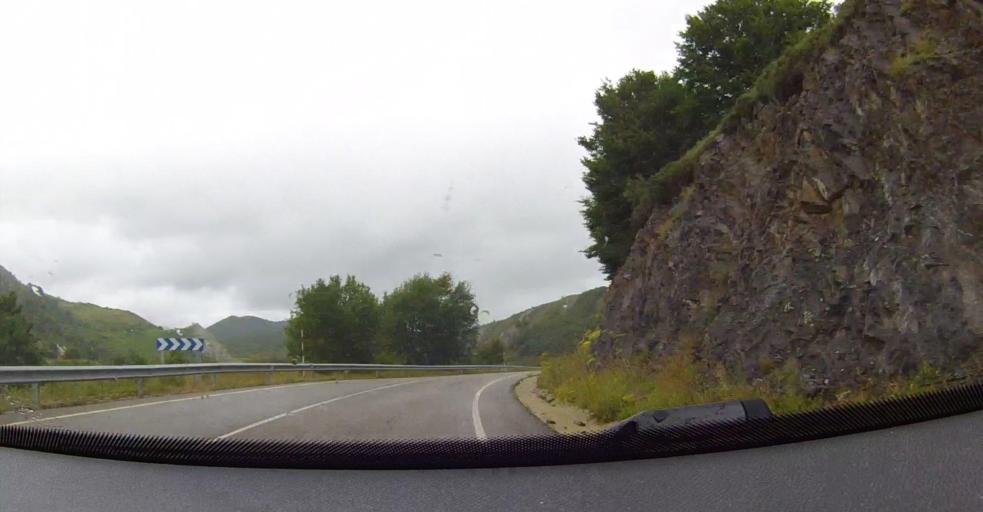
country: ES
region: Castille and Leon
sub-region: Provincia de Leon
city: Marana
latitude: 43.0724
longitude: -5.1500
